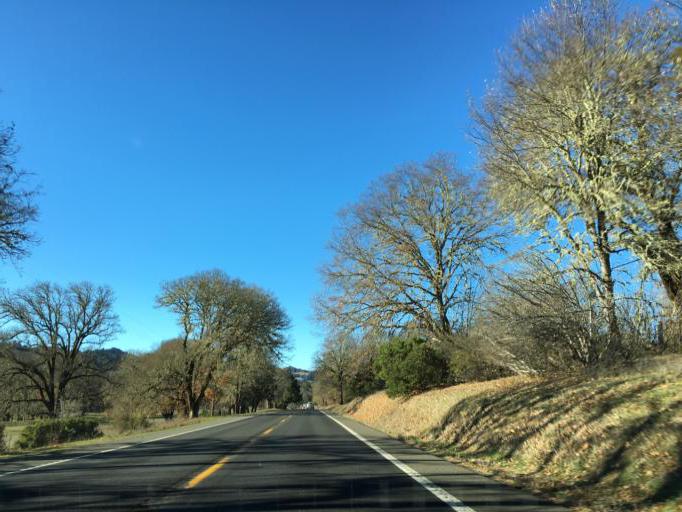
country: US
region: California
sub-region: Mendocino County
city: Laytonville
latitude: 39.7427
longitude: -123.5189
